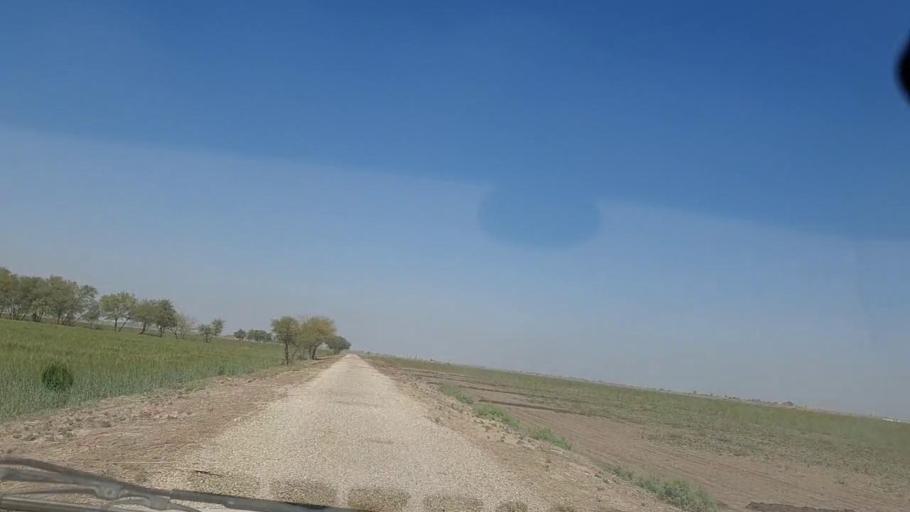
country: PK
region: Sindh
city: Mirpur Khas
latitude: 25.4360
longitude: 69.0510
